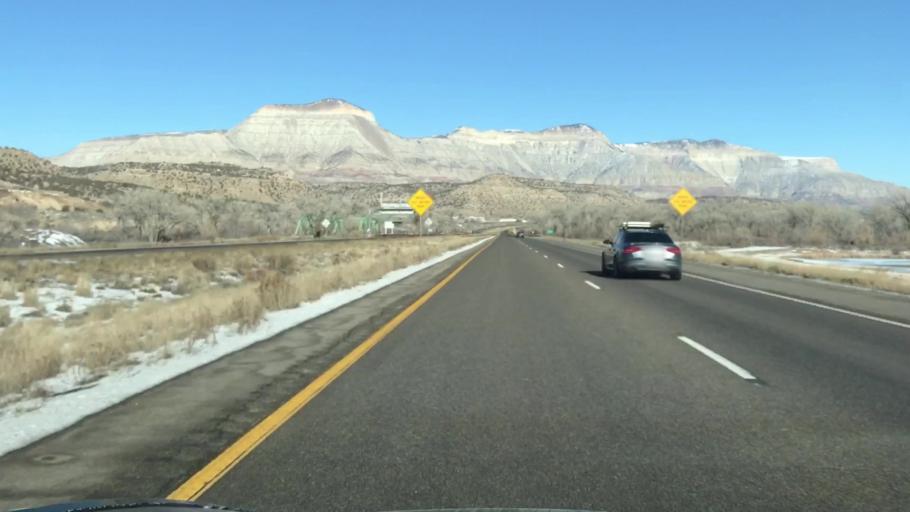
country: US
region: Colorado
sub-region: Garfield County
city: Parachute
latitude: 39.3356
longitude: -108.1940
